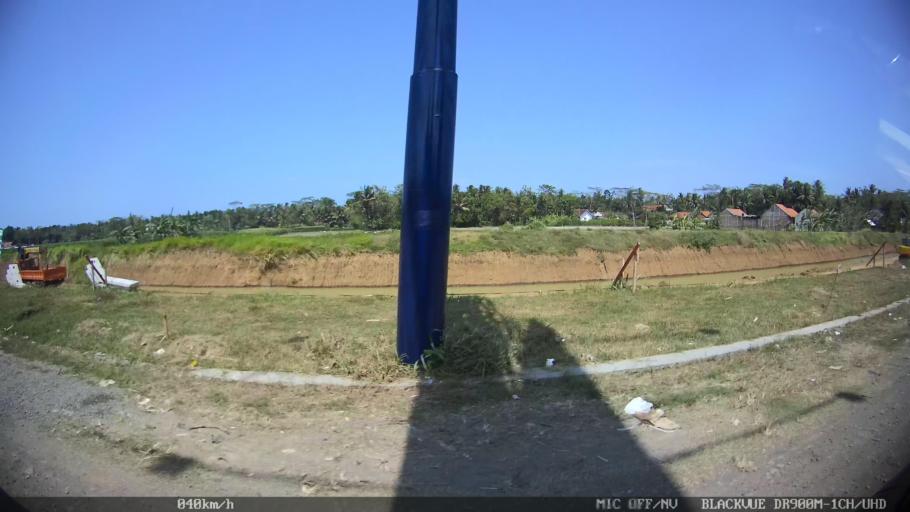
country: ID
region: Daerah Istimewa Yogyakarta
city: Srandakan
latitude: -7.8850
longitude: 110.0499
